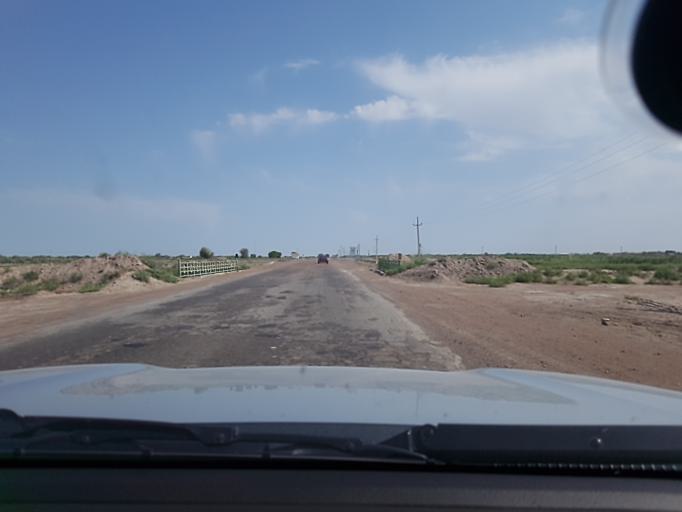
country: TM
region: Dasoguz
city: Boldumsaz
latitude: 42.1753
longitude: 59.5785
